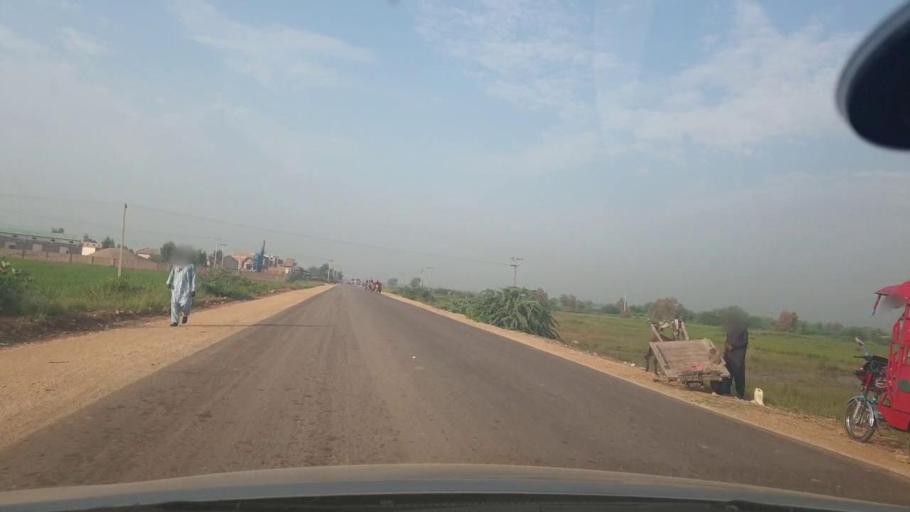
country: PK
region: Sindh
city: Jacobabad
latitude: 28.2616
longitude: 68.4155
